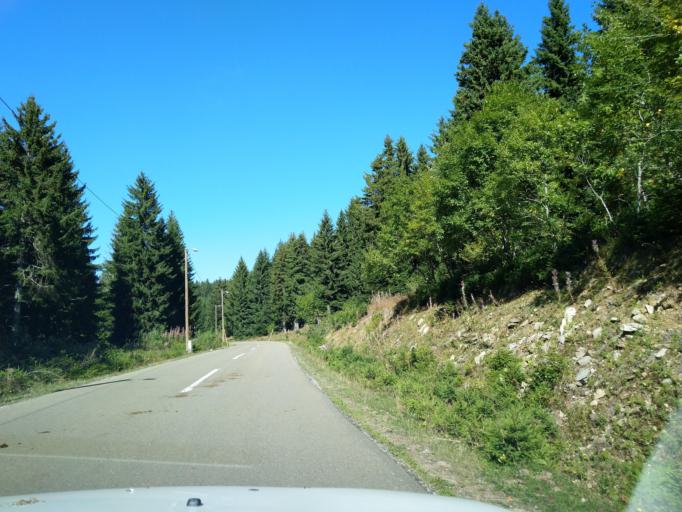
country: RS
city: Sokolovica
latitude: 43.2726
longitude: 20.3480
